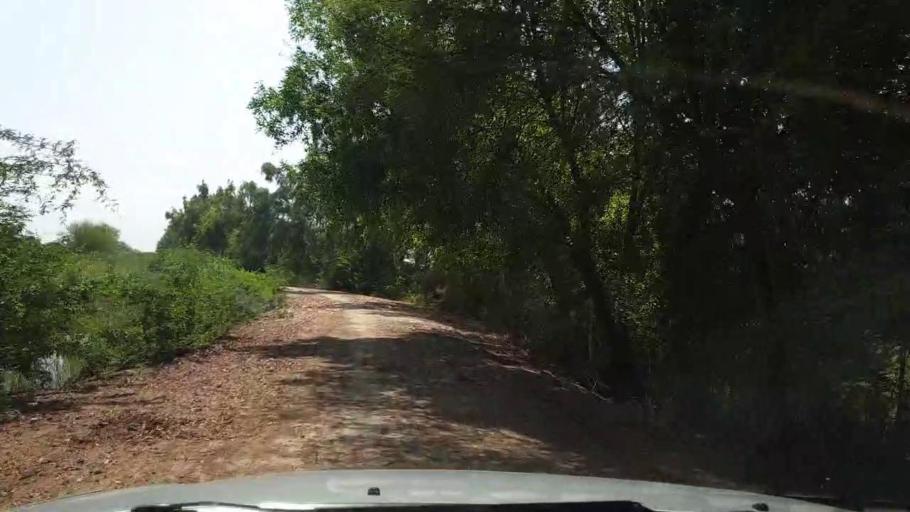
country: PK
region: Sindh
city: Rajo Khanani
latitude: 25.0099
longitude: 68.8577
